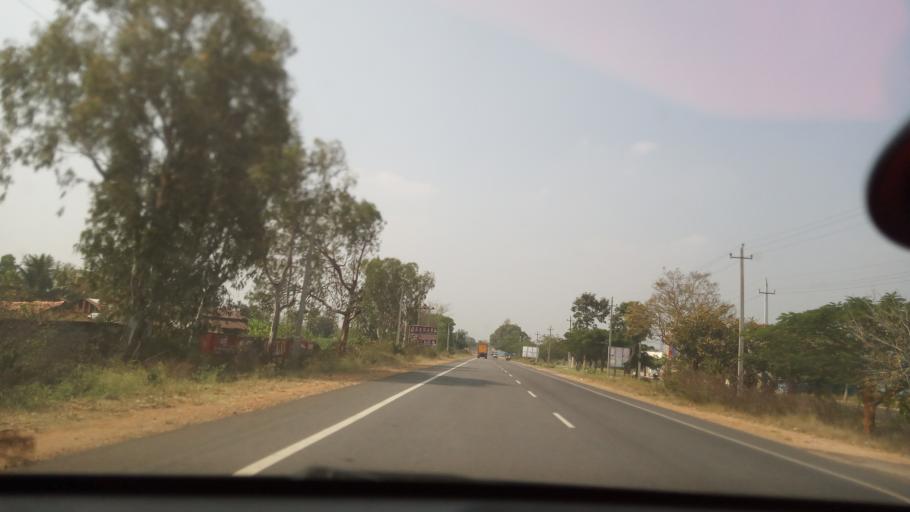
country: IN
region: Karnataka
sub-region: Mysore
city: Nanjangud
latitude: 12.0969
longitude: 76.7188
